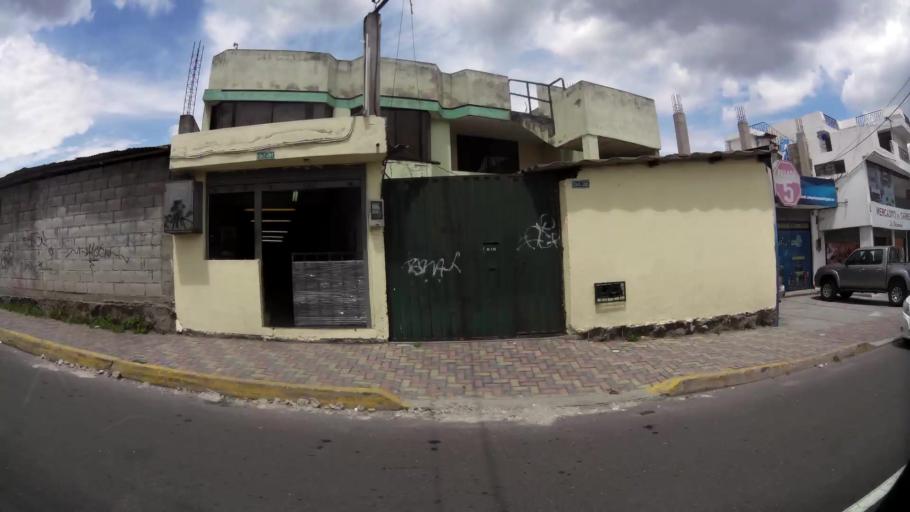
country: EC
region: Pichincha
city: Quito
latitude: -0.0972
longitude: -78.4418
